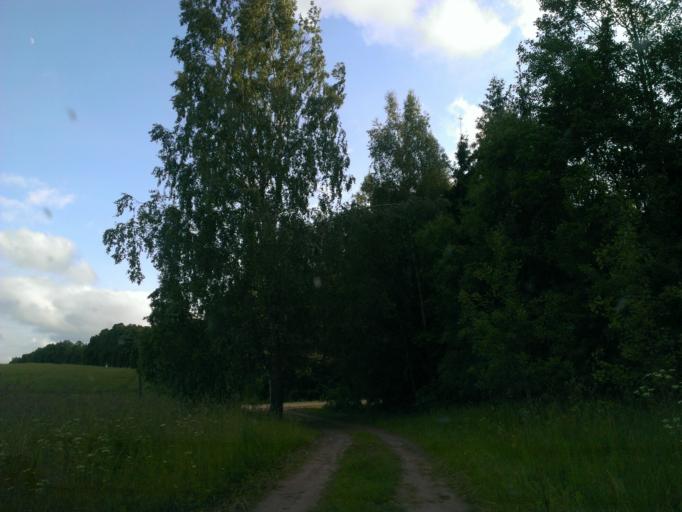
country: LV
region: Skrunda
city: Skrunda
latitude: 56.6909
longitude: 21.8735
